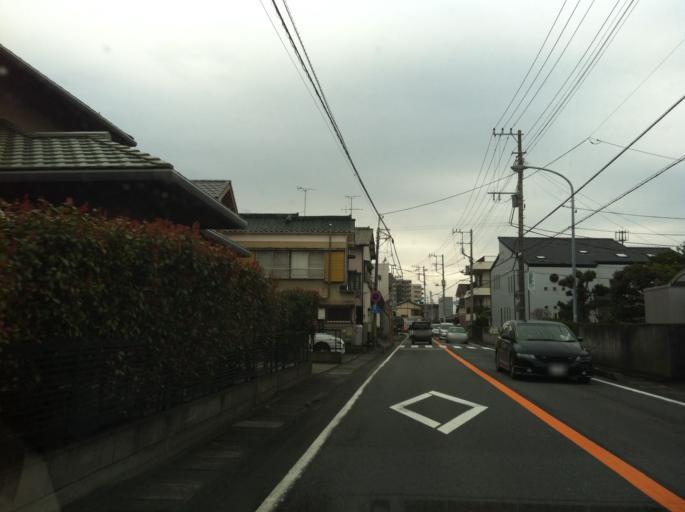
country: JP
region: Shizuoka
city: Numazu
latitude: 35.0660
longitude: 138.8782
